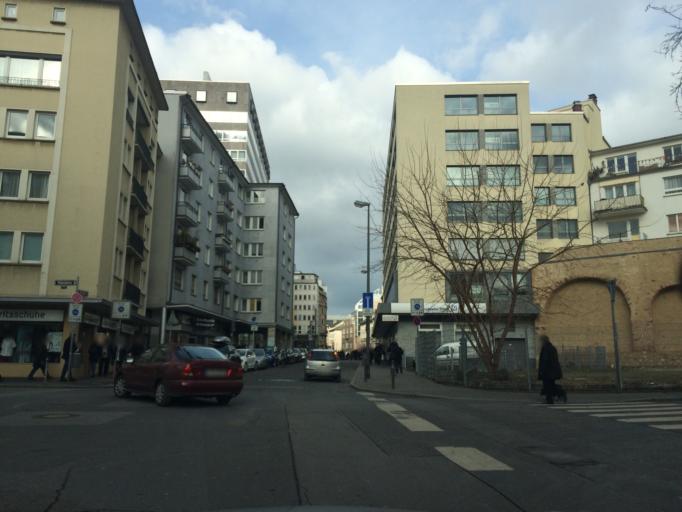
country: DE
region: Hesse
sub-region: Regierungsbezirk Darmstadt
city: Frankfurt am Main
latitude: 50.1134
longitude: 8.6862
